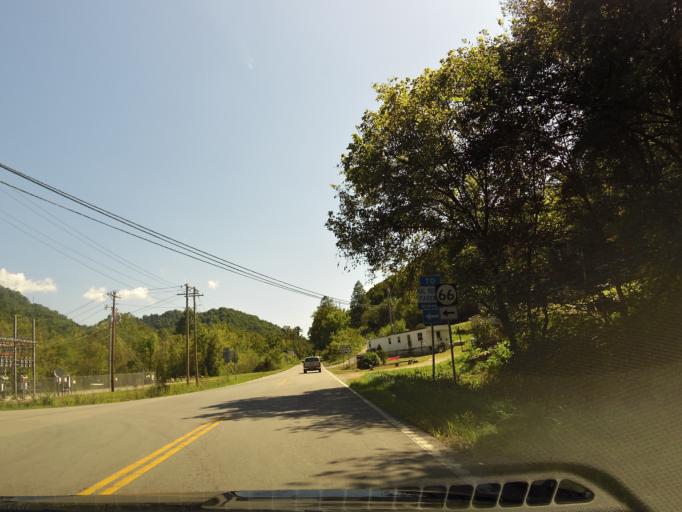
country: US
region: Kentucky
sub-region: Clay County
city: Manchester
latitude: 37.1640
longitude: -83.5813
